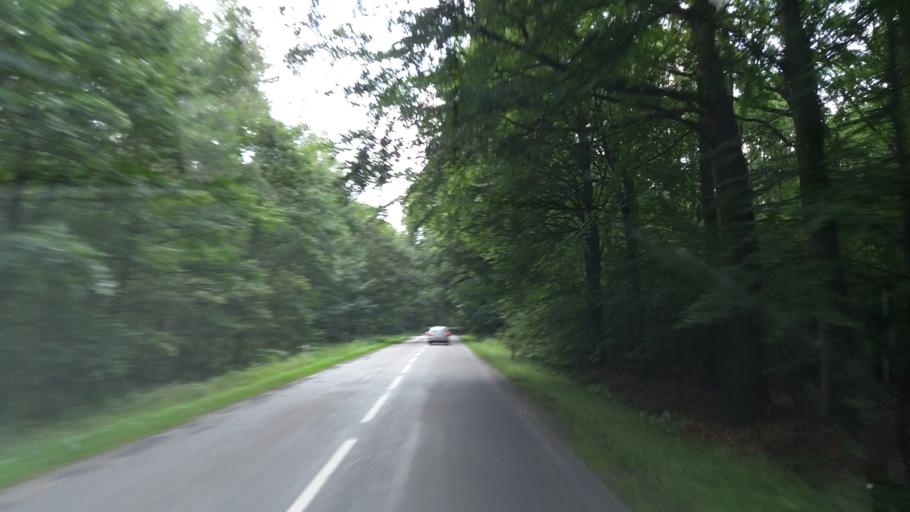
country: PL
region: West Pomeranian Voivodeship
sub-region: Powiat choszczenski
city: Pelczyce
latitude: 53.0726
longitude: 15.2920
